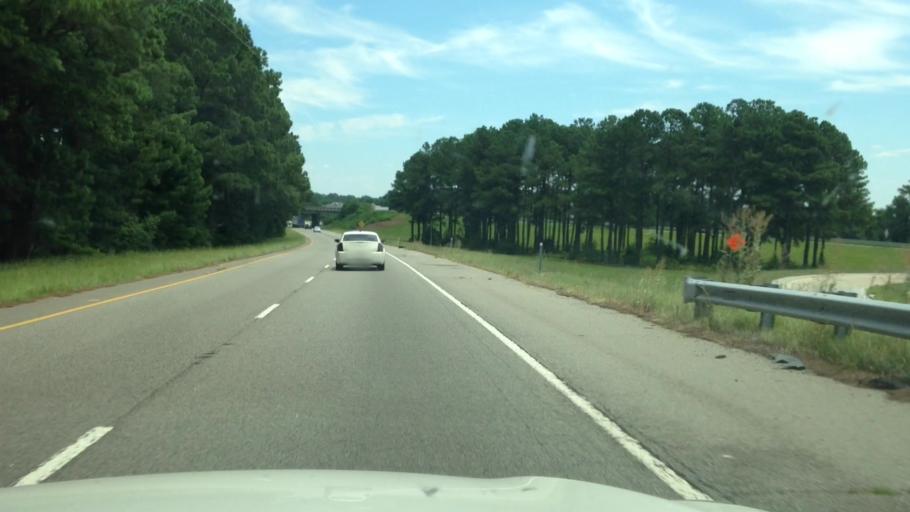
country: US
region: South Carolina
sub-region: Florence County
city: Florence
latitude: 34.1952
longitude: -79.8446
